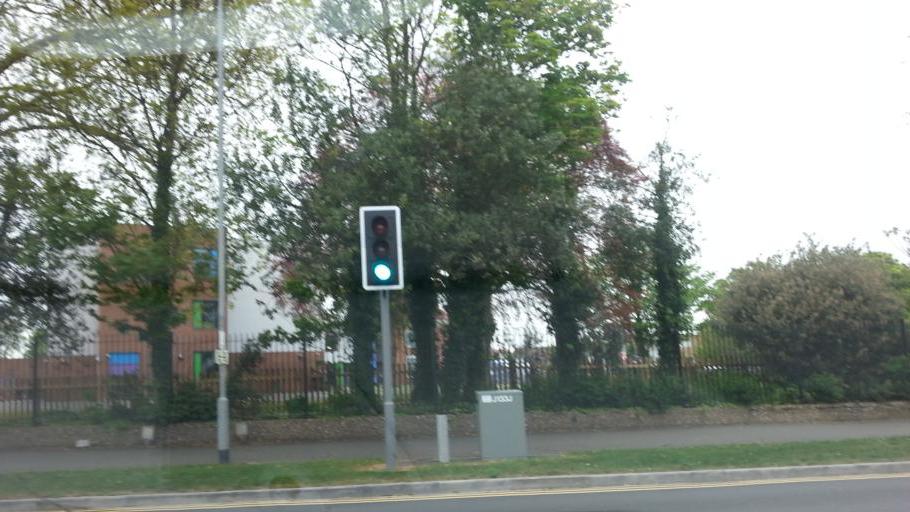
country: GB
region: England
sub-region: Peterborough
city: Peterborough
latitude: 52.5724
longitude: -0.2534
